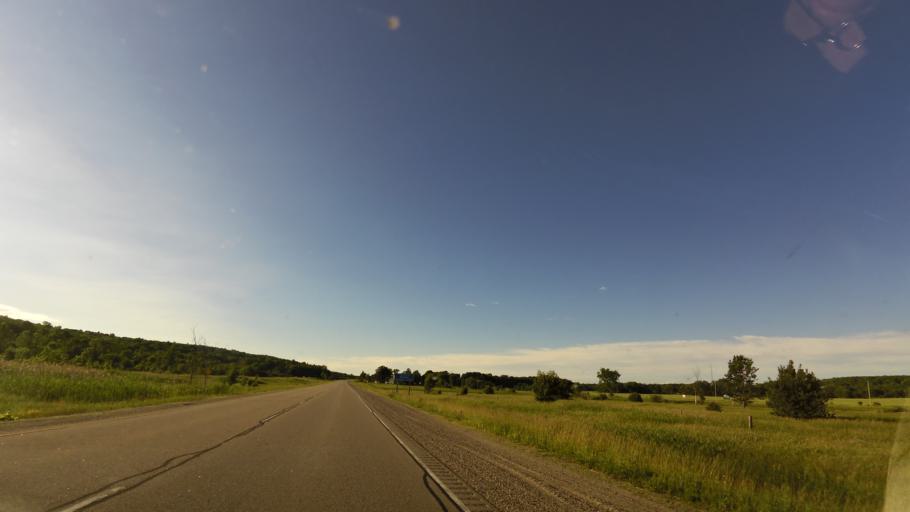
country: CA
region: Ontario
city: Orillia
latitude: 44.6761
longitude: -79.6449
